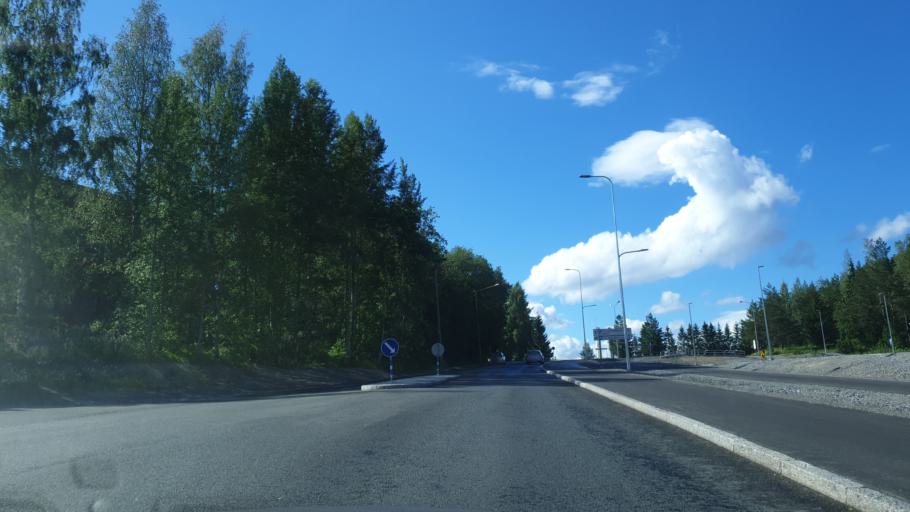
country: FI
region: Northern Savo
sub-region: Kuopio
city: Kuopio
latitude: 62.9050
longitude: 27.6540
